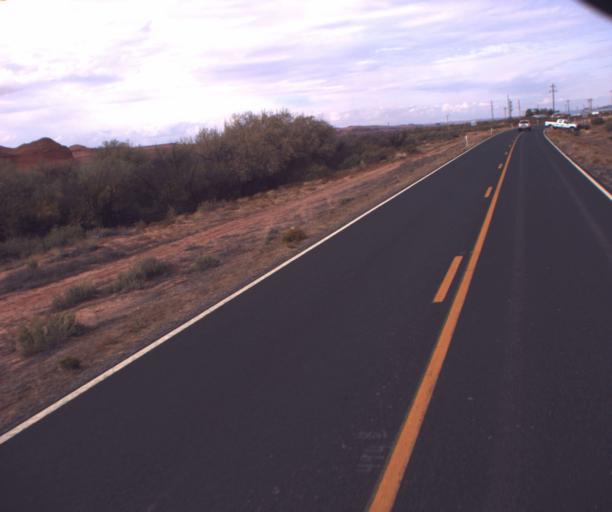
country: US
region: Arizona
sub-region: Apache County
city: Many Farms
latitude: 36.7128
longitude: -109.6248
